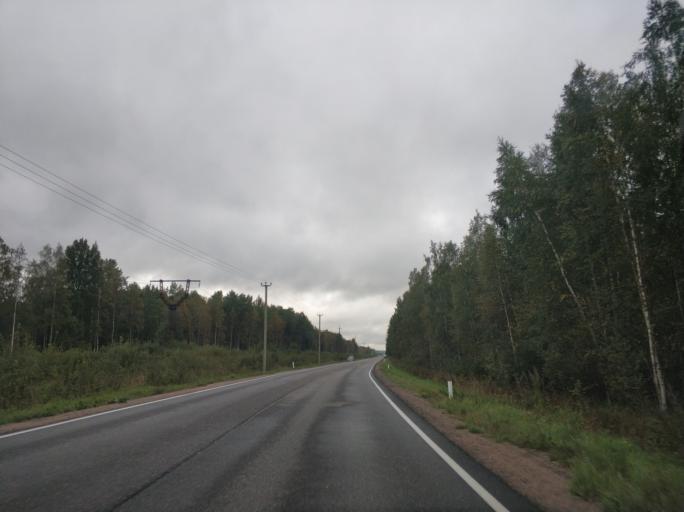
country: RU
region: Leningrad
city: Borisova Griva
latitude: 60.1142
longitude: 30.9633
